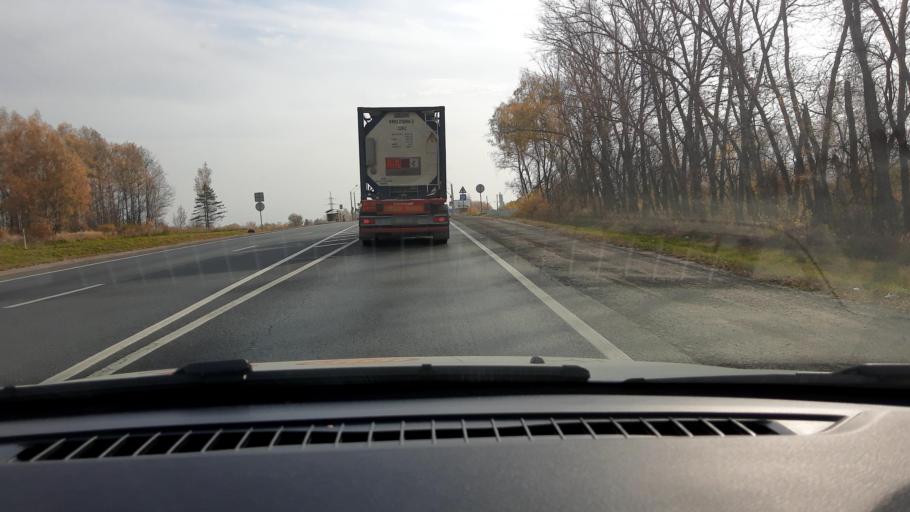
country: RU
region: Nizjnij Novgorod
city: Kstovo
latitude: 56.1127
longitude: 44.2814
